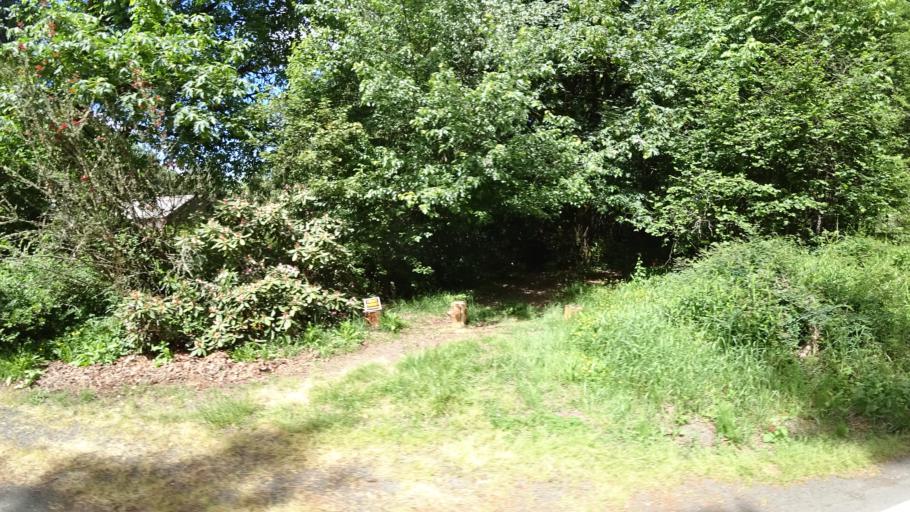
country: US
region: Oregon
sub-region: Washington County
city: Oak Hills
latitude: 45.5886
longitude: -122.8071
